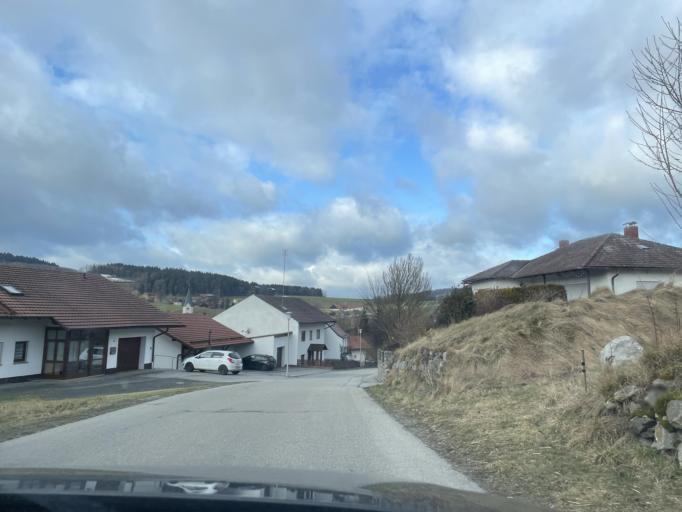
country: DE
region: Bavaria
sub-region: Lower Bavaria
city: Prackenbach
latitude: 49.0934
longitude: 12.8300
